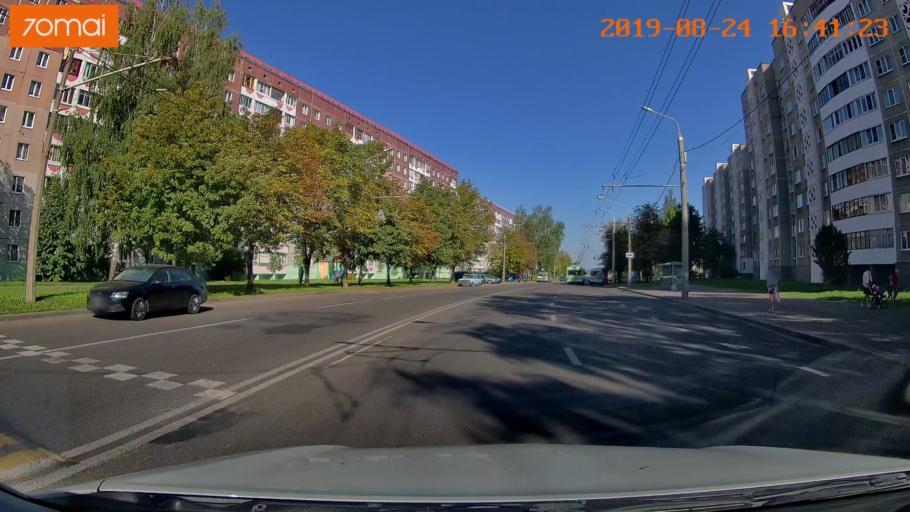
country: BY
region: Minsk
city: Syenitsa
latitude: 53.8516
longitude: 27.5490
